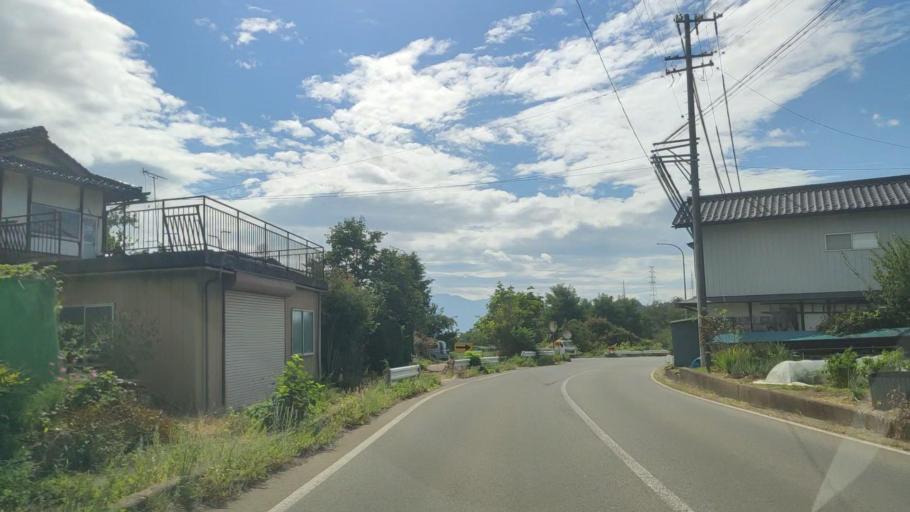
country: JP
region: Nagano
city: Nakano
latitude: 36.7429
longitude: 138.3088
